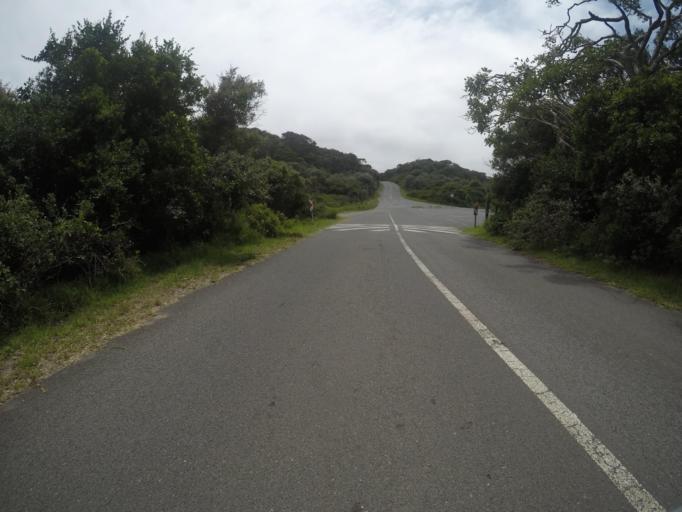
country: ZA
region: Eastern Cape
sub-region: Buffalo City Metropolitan Municipality
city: East London
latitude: -32.9959
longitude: 27.9471
